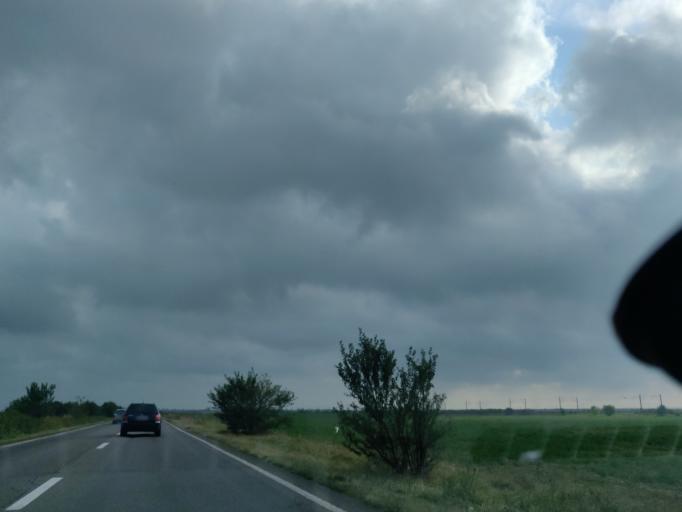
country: RO
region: Prahova
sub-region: Oras Mizil
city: Mizil
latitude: 45.0141
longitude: 26.4728
